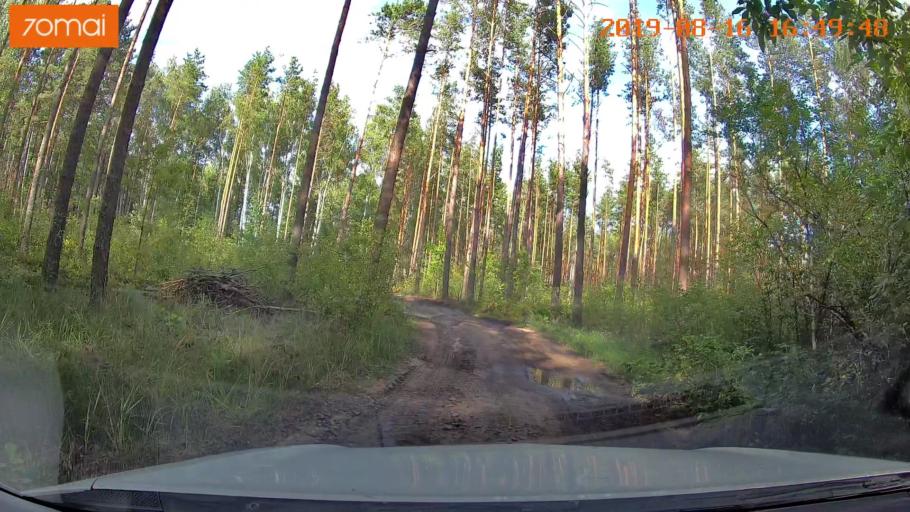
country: BY
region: Mogilev
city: Asipovichy
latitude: 53.2505
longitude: 28.7978
